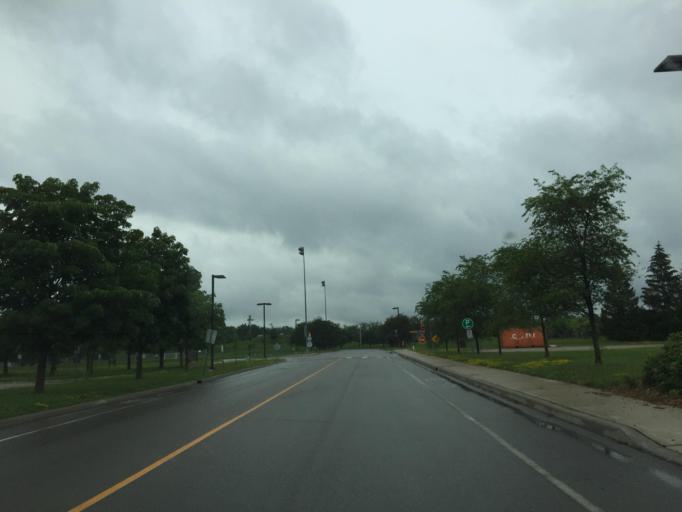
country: CA
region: Ontario
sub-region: Wellington County
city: Guelph
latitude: 43.5333
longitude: -80.2188
